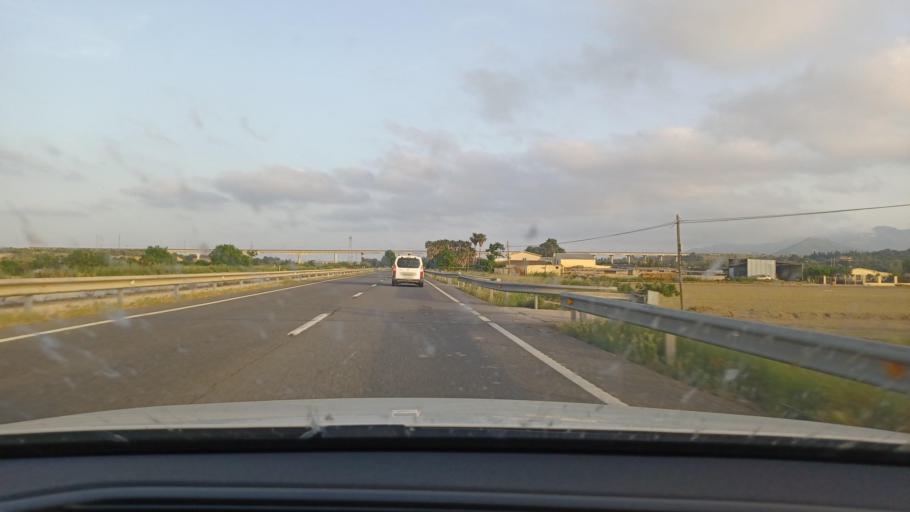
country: ES
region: Catalonia
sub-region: Provincia de Tarragona
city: Amposta
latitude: 40.7389
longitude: 0.5657
